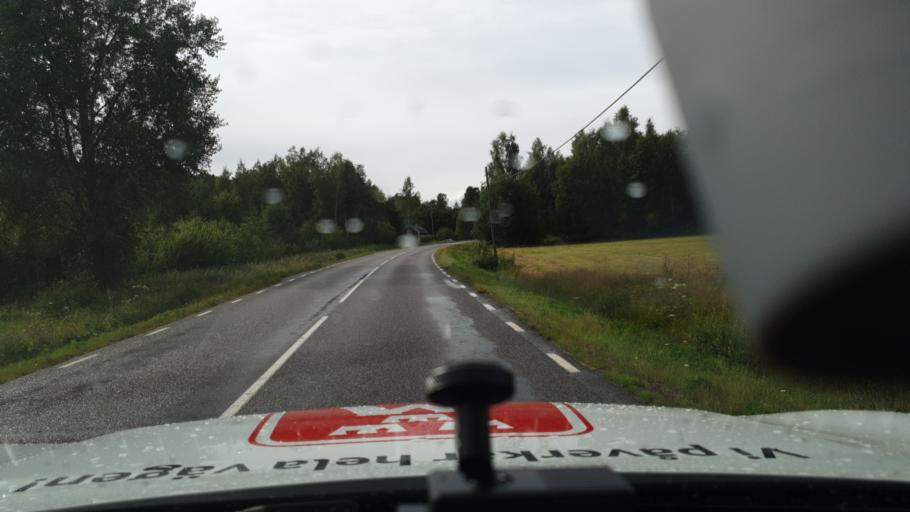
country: SE
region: Vaermland
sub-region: Sunne Kommun
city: Sunne
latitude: 59.8069
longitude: 13.0355
